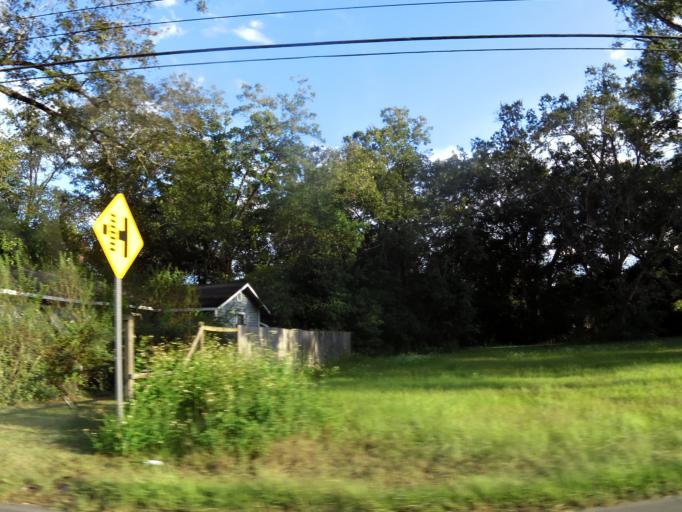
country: US
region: Georgia
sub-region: Lowndes County
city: Valdosta
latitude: 30.8213
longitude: -83.2999
